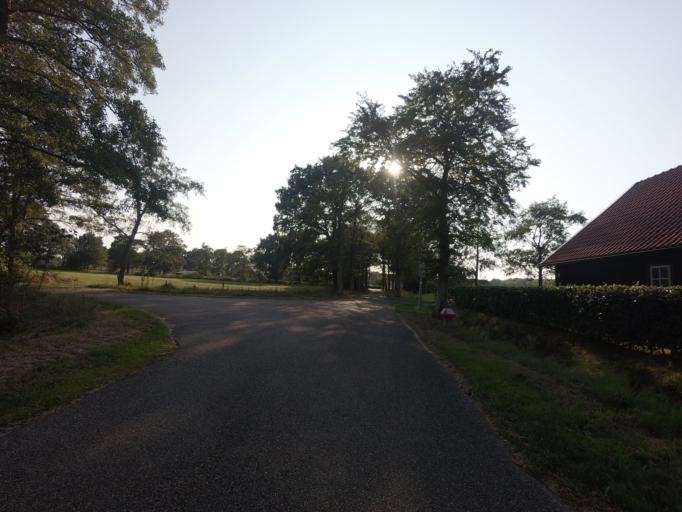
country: NL
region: Drenthe
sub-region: Gemeente Tynaarlo
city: Vries
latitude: 53.1317
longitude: 6.4897
